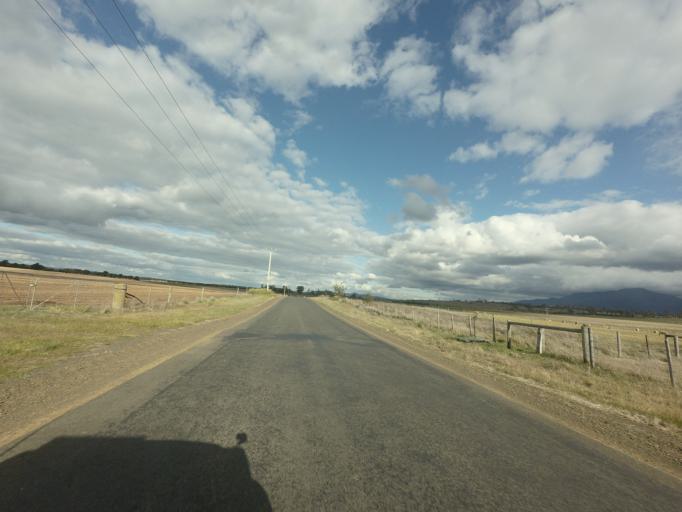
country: AU
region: Tasmania
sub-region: Northern Midlands
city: Longford
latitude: -41.8108
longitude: 147.1874
